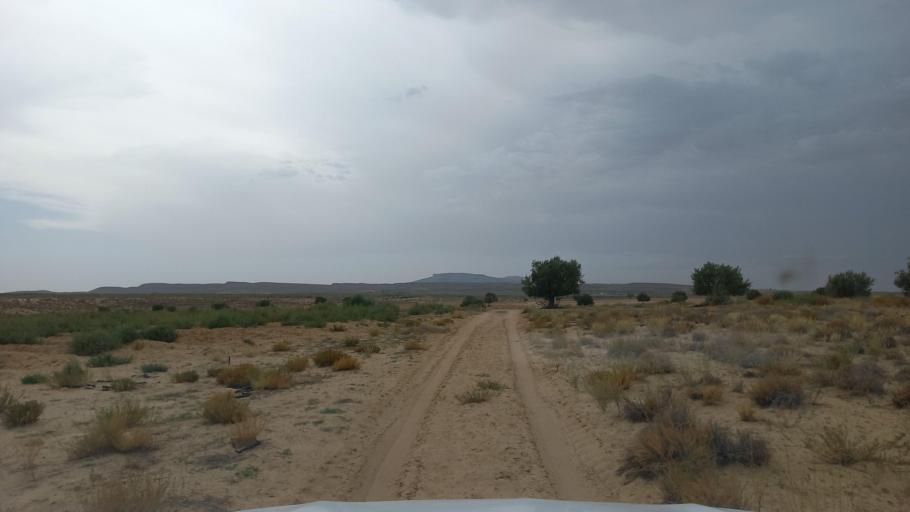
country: TN
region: Al Qasrayn
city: Kasserine
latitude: 35.2340
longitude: 9.0141
